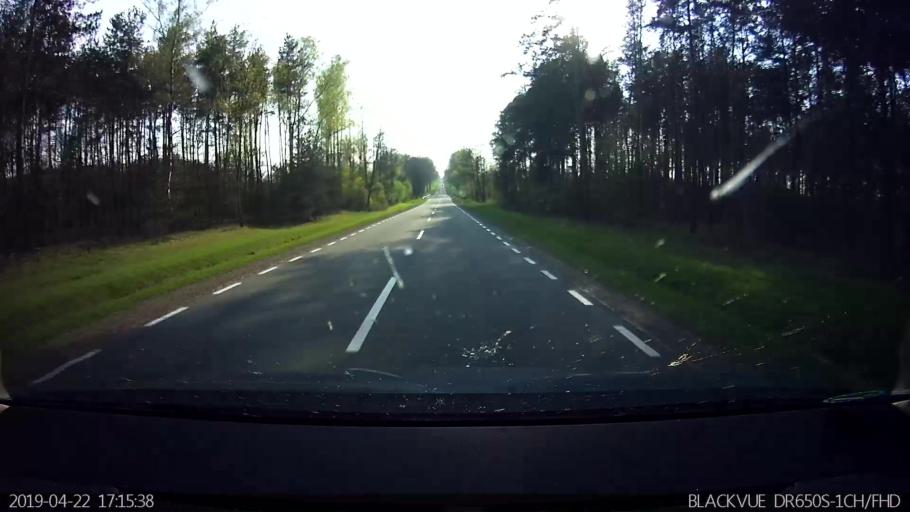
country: PL
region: Masovian Voivodeship
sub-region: Powiat sokolowski
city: Jablonna Lacka
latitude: 52.3997
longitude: 22.4822
